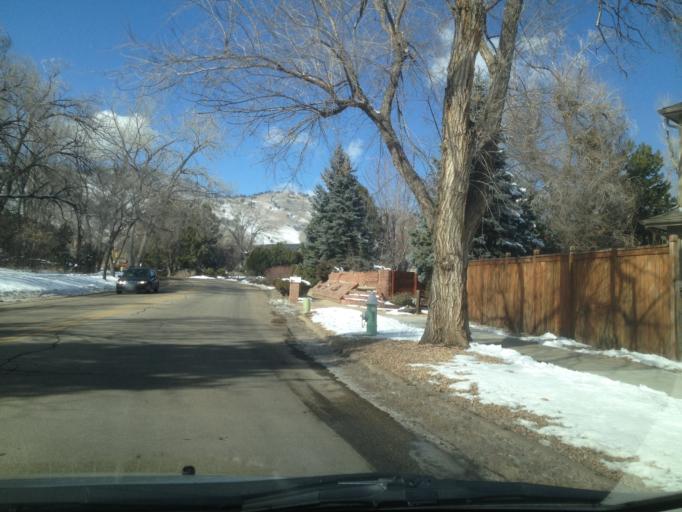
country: US
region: Colorado
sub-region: Boulder County
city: Boulder
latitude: 40.0465
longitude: -105.2856
